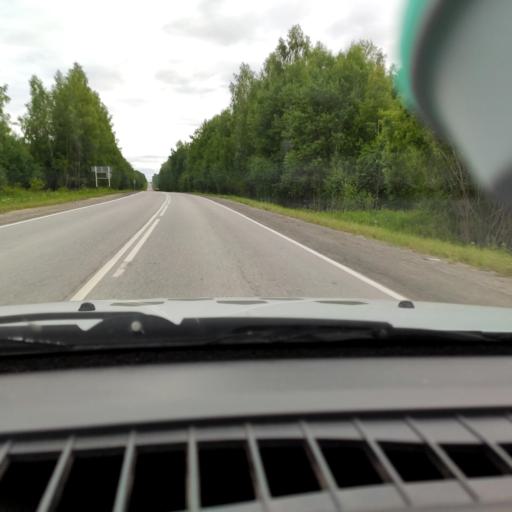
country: RU
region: Perm
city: Lys'va
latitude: 58.1520
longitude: 57.7619
